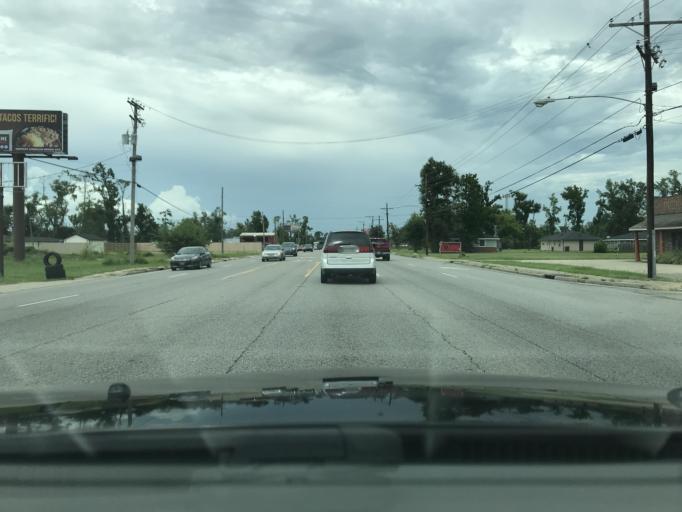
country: US
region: Louisiana
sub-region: Calcasieu Parish
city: Moss Bluff
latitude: 30.2596
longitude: -93.1806
